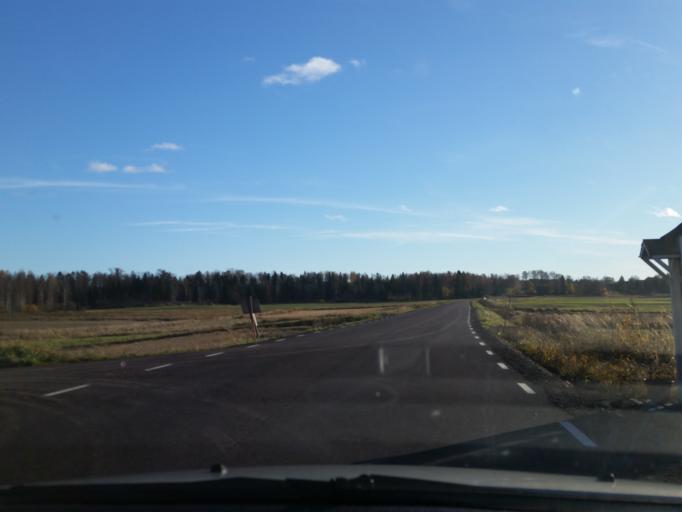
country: AX
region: Alands landsbygd
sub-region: Jomala
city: Jomala
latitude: 60.1962
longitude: 19.9585
